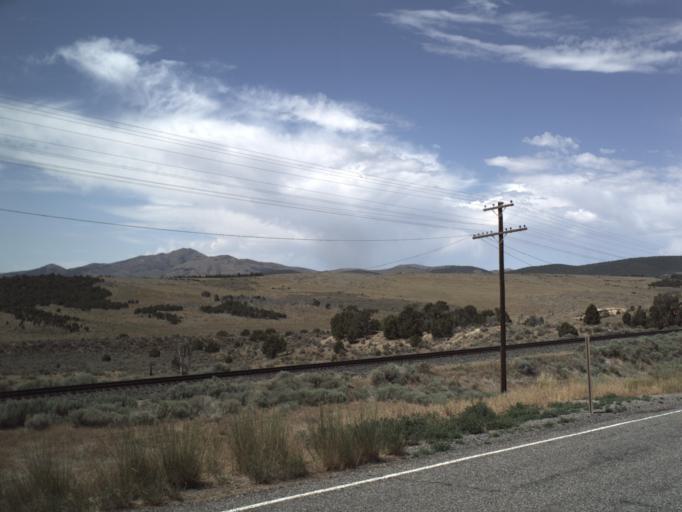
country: US
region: Utah
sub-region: Utah County
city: Genola
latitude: 39.9446
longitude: -112.2208
